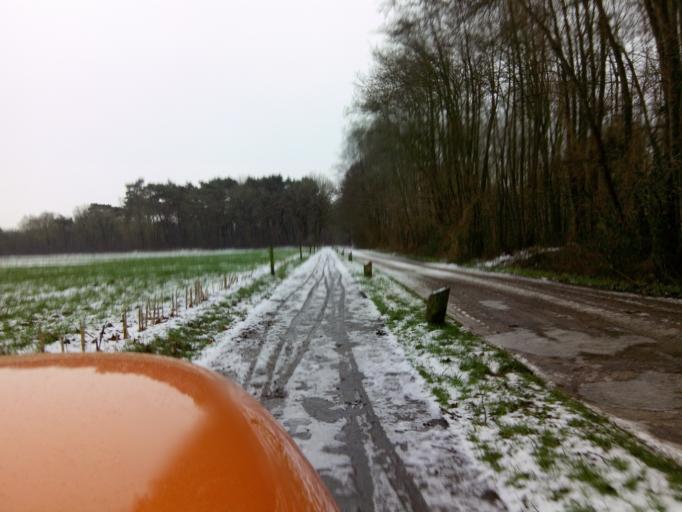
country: NL
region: Gelderland
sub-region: Gemeente Putten
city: Putten
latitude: 52.2291
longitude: 5.5597
